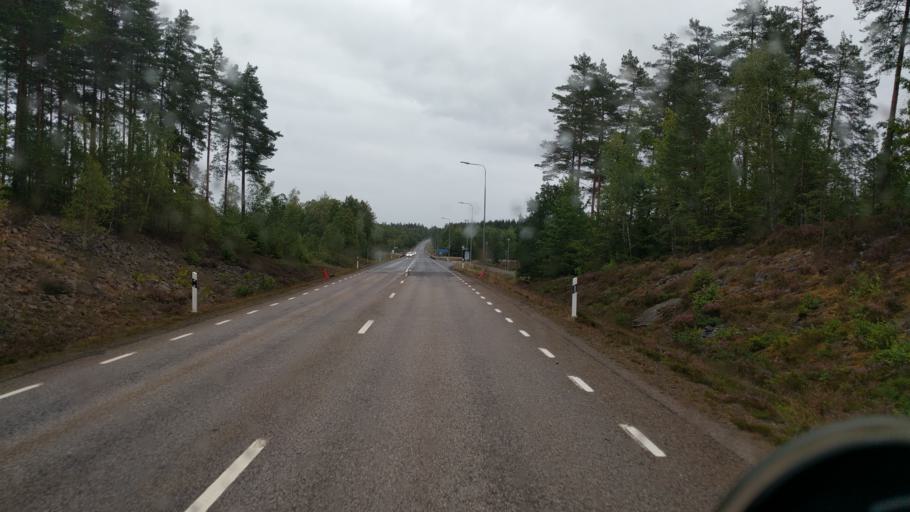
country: SE
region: Kalmar
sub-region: Vasterviks Kommun
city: Ankarsrum
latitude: 57.7064
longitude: 16.3271
